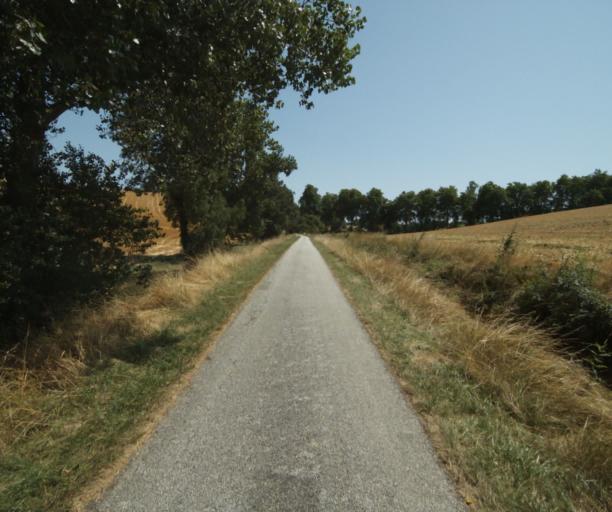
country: FR
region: Midi-Pyrenees
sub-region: Departement de la Haute-Garonne
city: Saint-Felix-Lauragais
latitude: 43.4632
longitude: 1.8565
